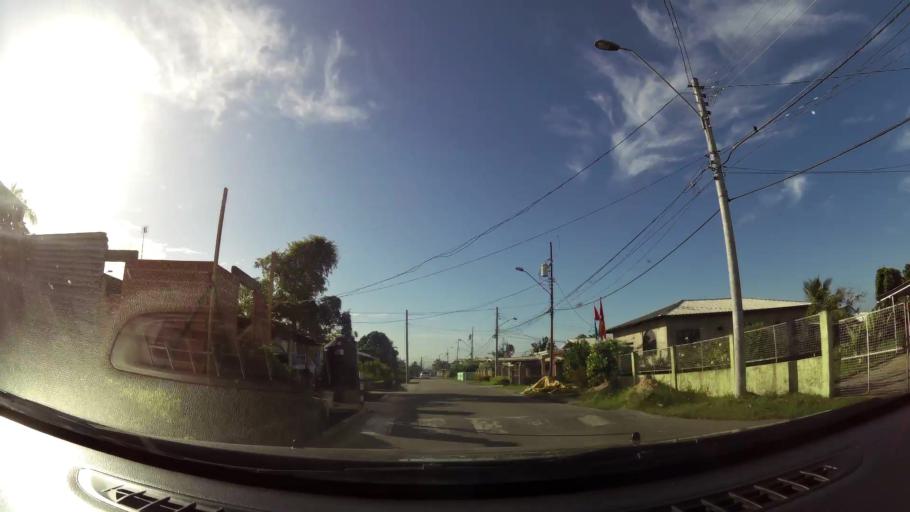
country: TT
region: Tunapuna/Piarco
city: Tunapuna
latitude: 10.5775
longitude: -61.3811
